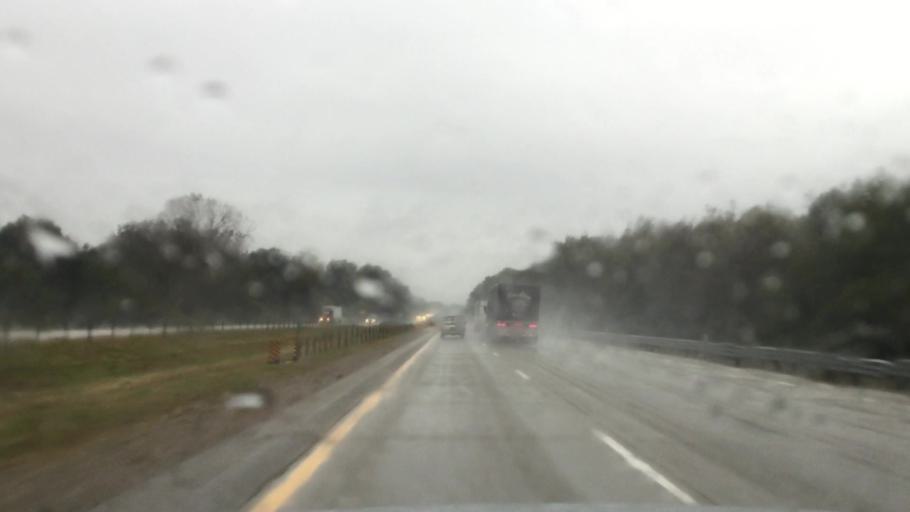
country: US
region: Michigan
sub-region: Van Buren County
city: Paw Paw
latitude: 42.1974
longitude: -85.9731
